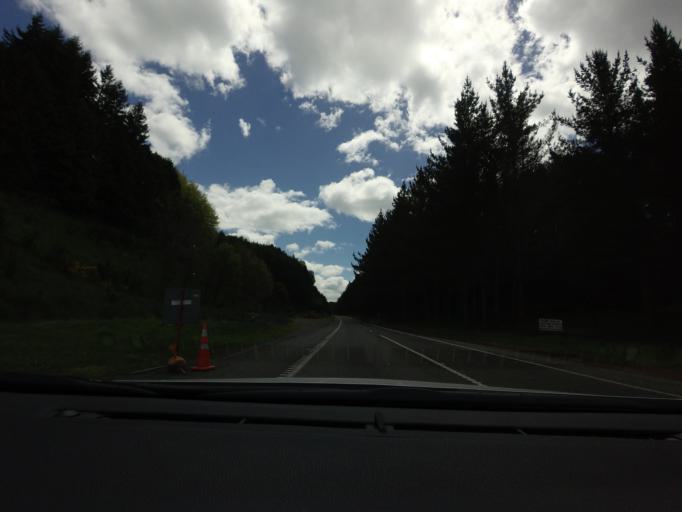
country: NZ
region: Bay of Plenty
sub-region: Rotorua District
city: Rotorua
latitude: -38.2445
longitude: 176.3108
